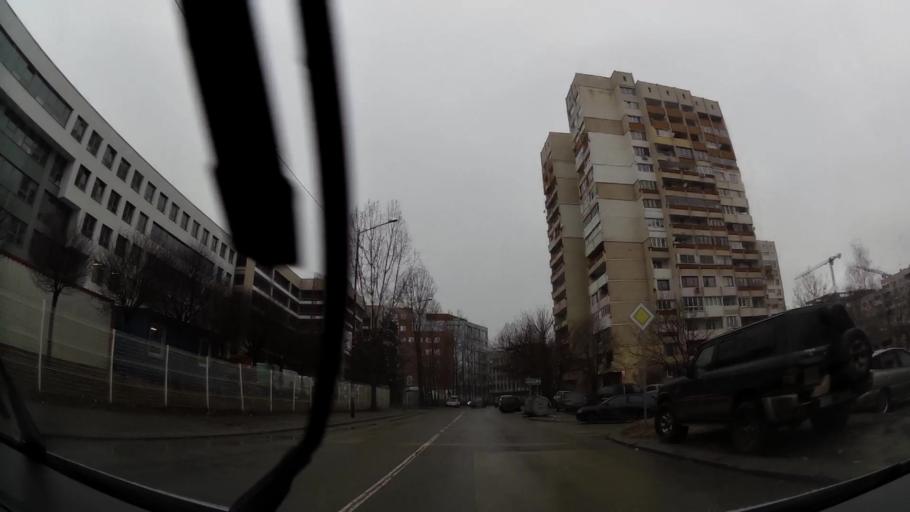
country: BG
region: Sofia-Capital
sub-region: Stolichna Obshtina
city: Sofia
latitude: 42.6272
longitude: 23.3768
